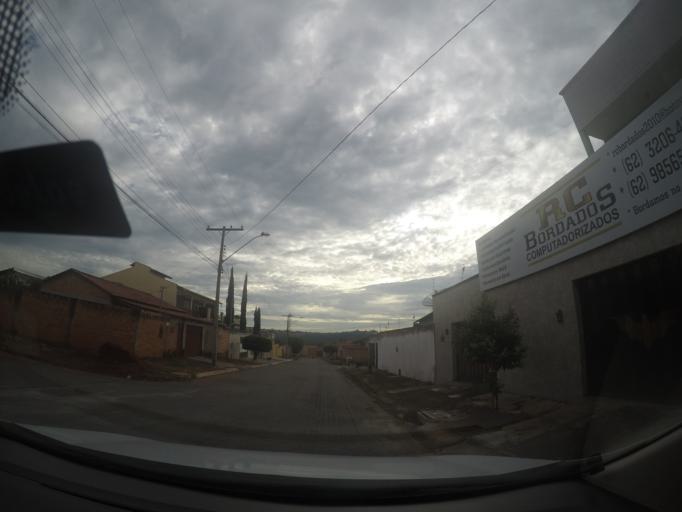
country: BR
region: Goias
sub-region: Goiania
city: Goiania
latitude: -16.6752
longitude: -49.2060
